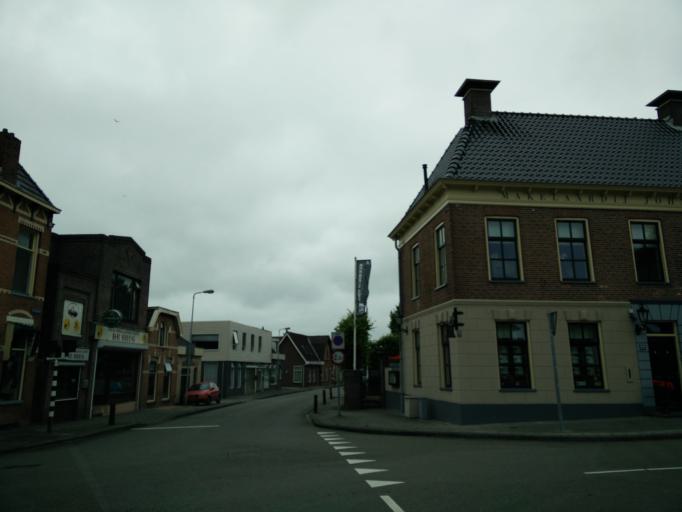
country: NL
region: Groningen
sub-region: Gemeente Zuidhorn
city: Aduard
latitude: 53.2160
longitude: 6.5006
